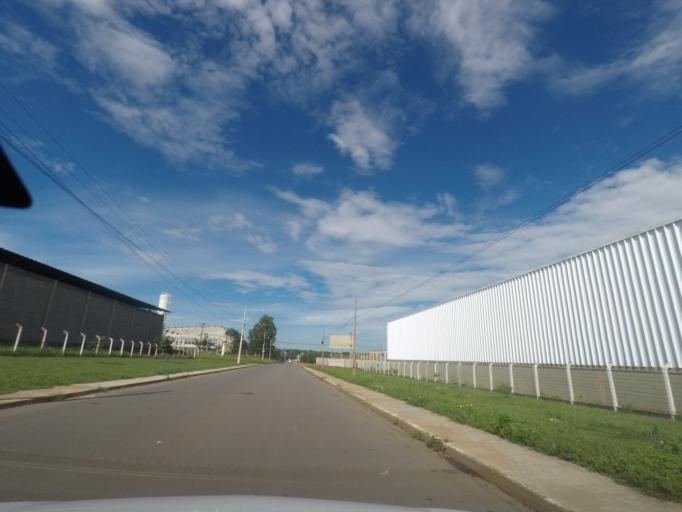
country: BR
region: Goias
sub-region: Aparecida De Goiania
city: Aparecida de Goiania
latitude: -16.7900
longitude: -49.2568
